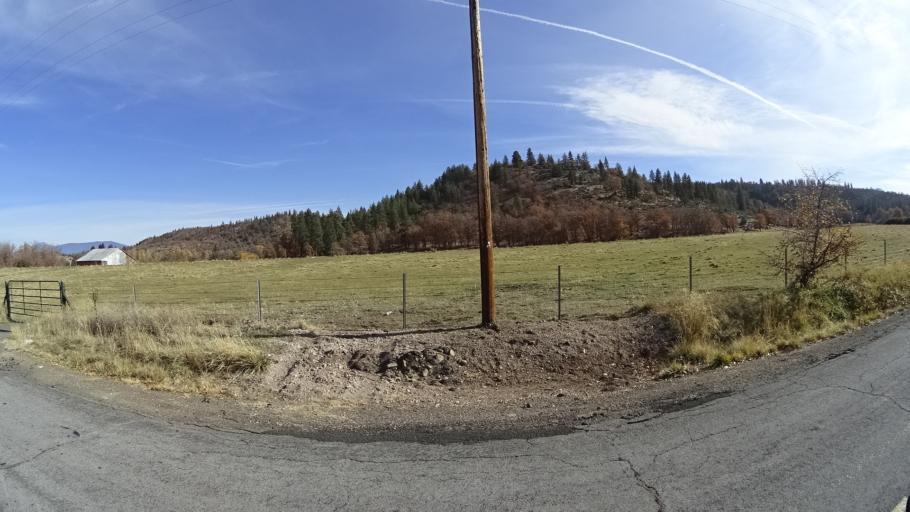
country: US
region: California
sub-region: Siskiyou County
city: Weed
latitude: 41.4497
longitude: -122.4306
